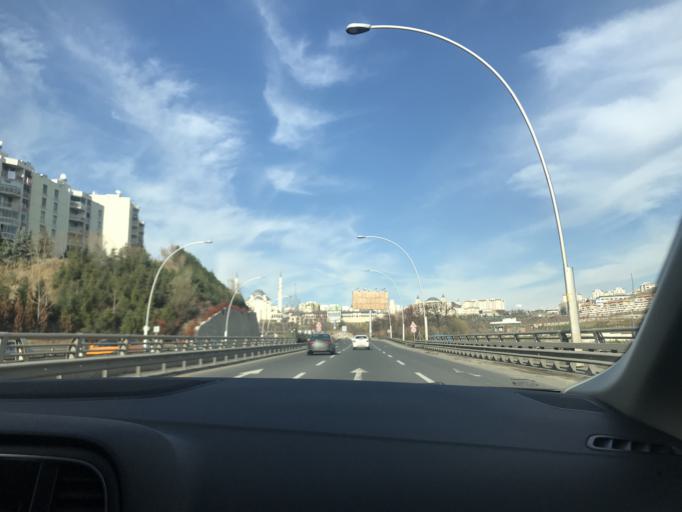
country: TR
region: Ankara
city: Mamak
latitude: 40.0003
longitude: 32.8946
